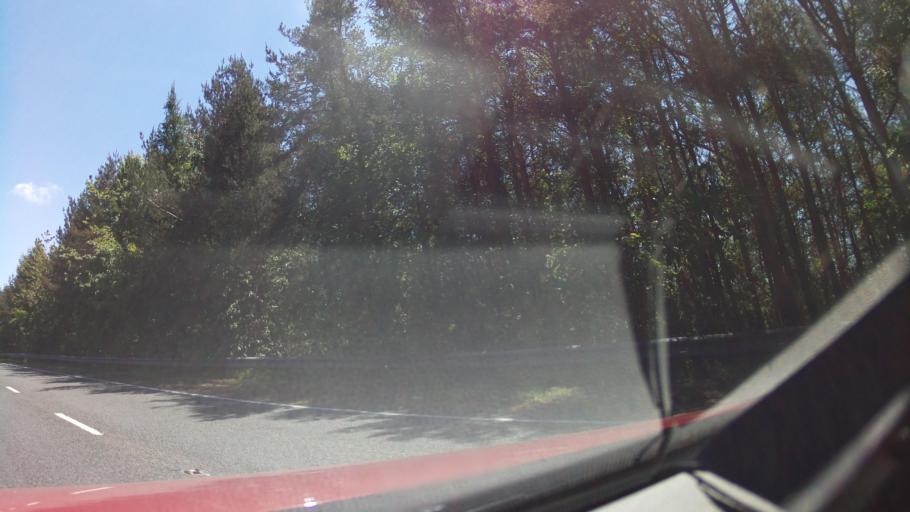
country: GB
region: Scotland
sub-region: The Scottish Borders
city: Hawick
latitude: 55.4765
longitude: -2.8141
